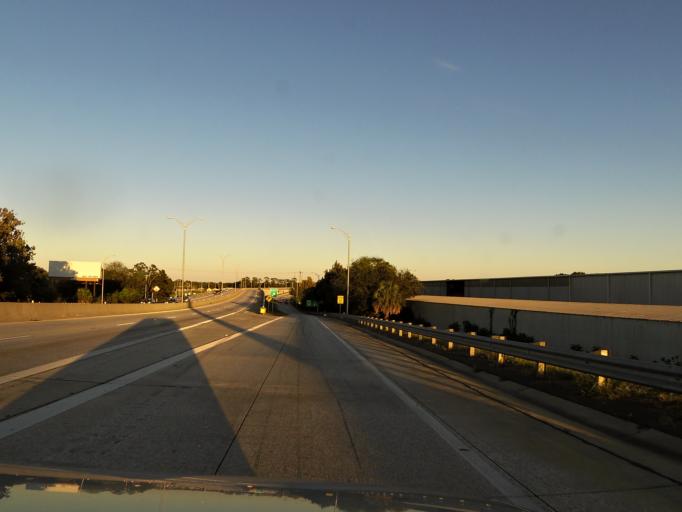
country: US
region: Florida
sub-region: Duval County
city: Jacksonville
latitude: 30.3561
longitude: -81.6446
